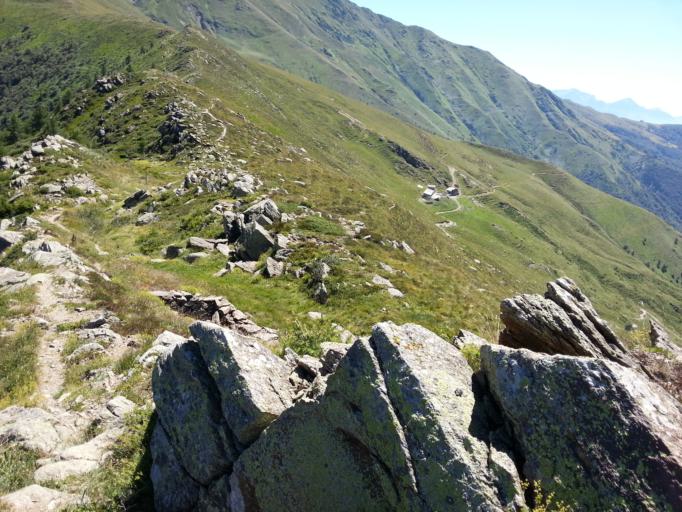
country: CH
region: Ticino
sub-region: Bellinzona District
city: Camorino
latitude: 46.1132
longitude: 9.0442
